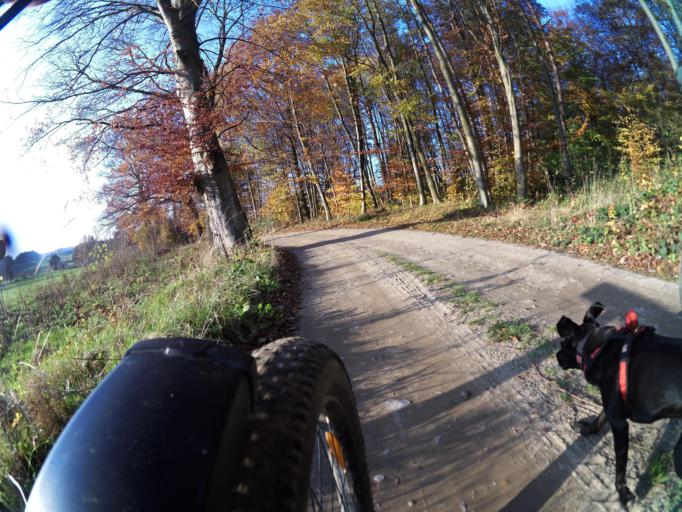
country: PL
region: Pomeranian Voivodeship
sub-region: Powiat pucki
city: Krokowa
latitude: 54.7497
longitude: 18.1961
